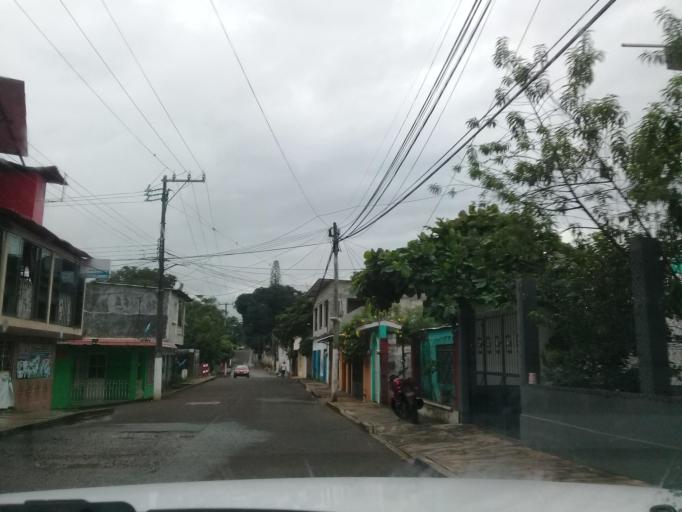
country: MX
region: Veracruz
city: San Andres Tuxtla
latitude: 18.4422
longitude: -95.2201
